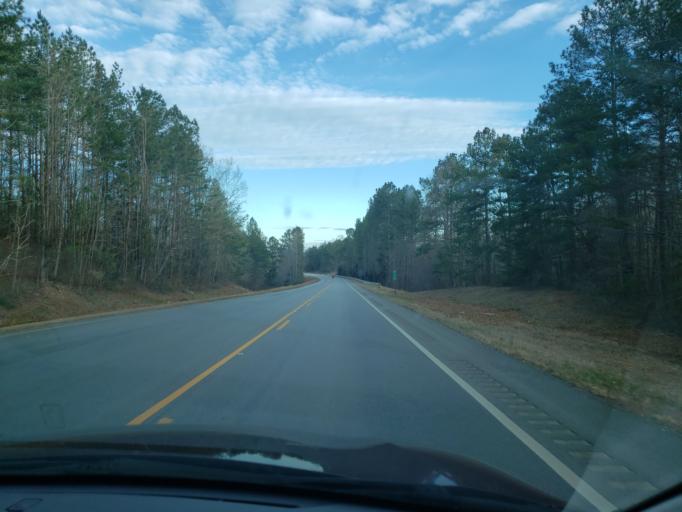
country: US
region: Alabama
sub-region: Randolph County
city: Wedowee
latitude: 33.3611
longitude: -85.4921
